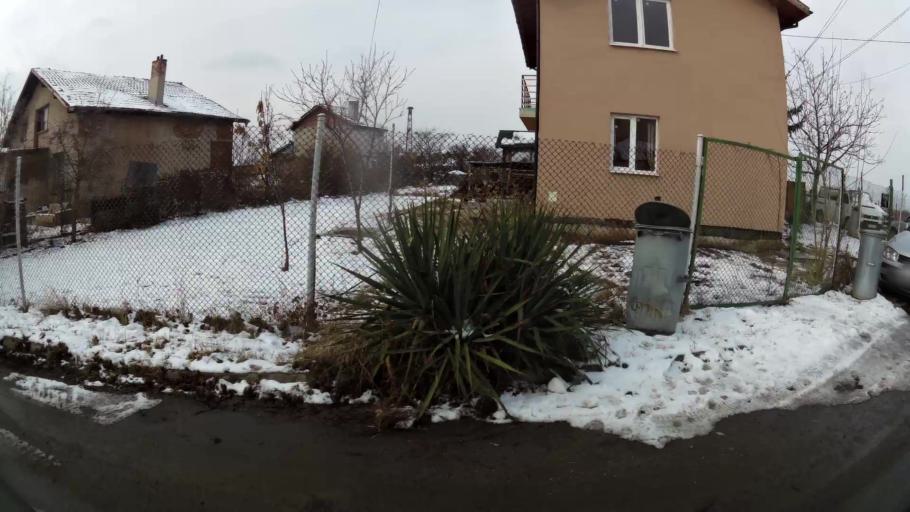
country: BG
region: Sofia-Capital
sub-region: Stolichna Obshtina
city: Sofia
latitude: 42.7156
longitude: 23.3999
